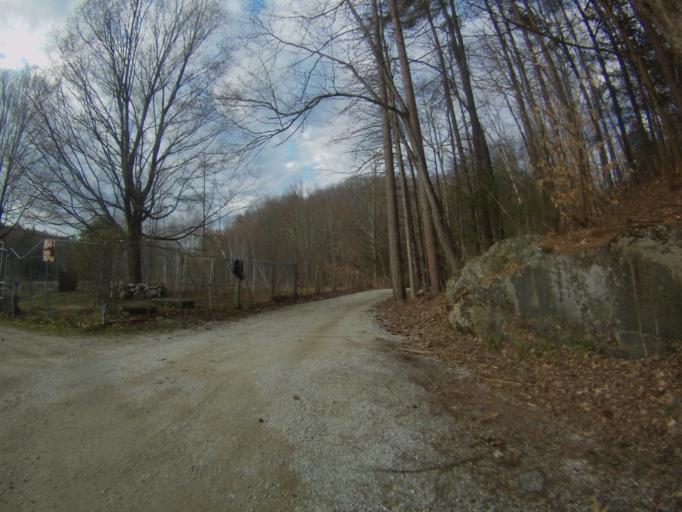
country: US
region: Vermont
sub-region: Rutland County
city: Brandon
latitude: 43.8380
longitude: -73.0409
